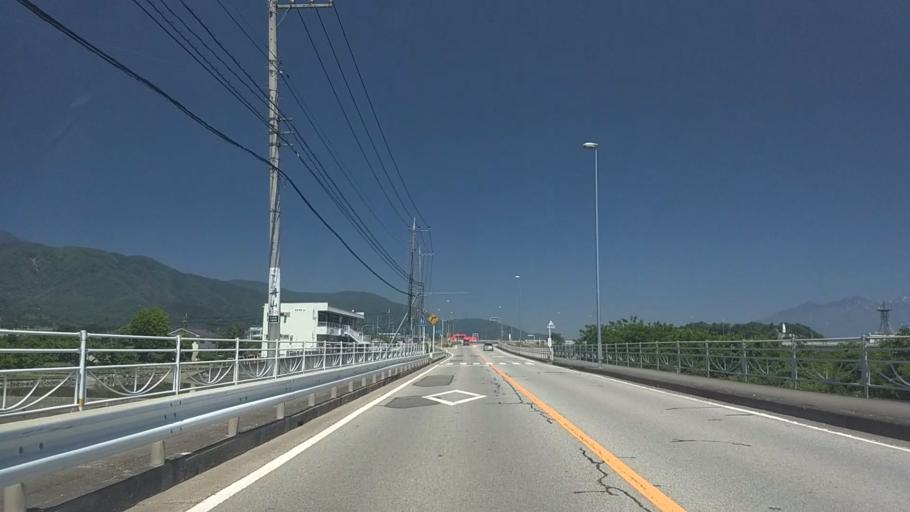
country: JP
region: Yamanashi
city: Nirasaki
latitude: 35.6976
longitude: 138.4552
